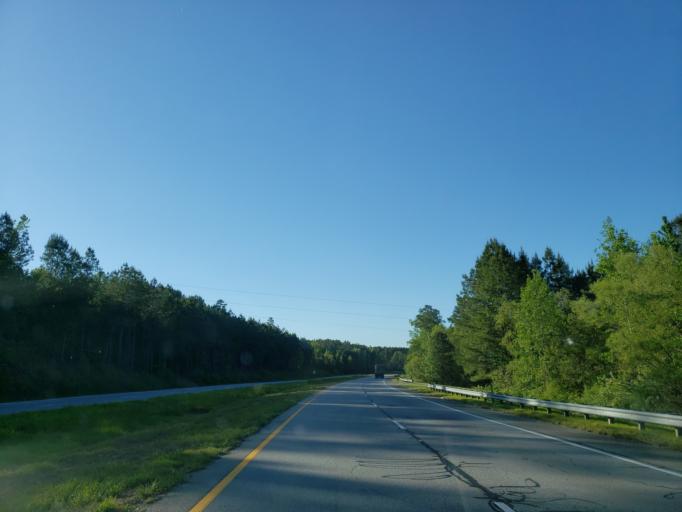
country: US
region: Georgia
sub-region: Haralson County
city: Buchanan
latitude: 33.8497
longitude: -85.2087
